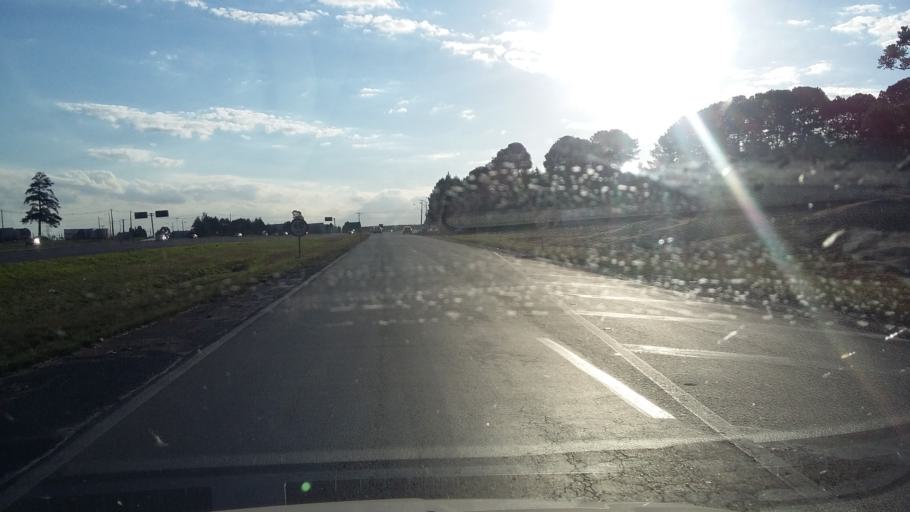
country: BR
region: Parana
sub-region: Sao Jose Dos Pinhais
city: Sao Jose dos Pinhais
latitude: -25.5438
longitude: -49.3046
